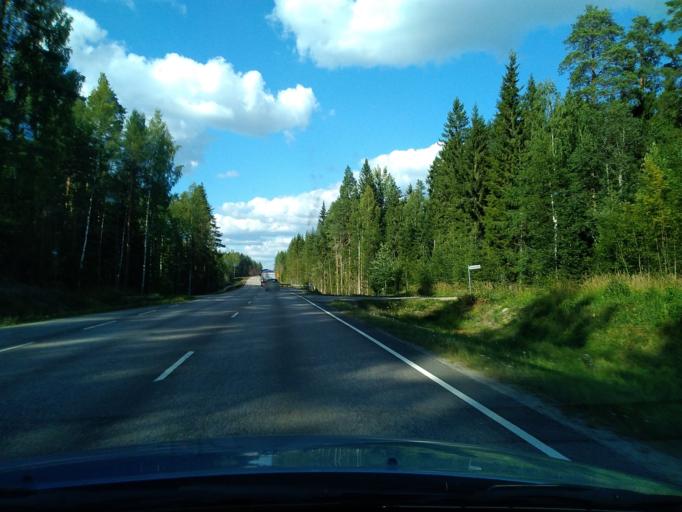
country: FI
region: Central Finland
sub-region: Keuruu
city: Keuruu
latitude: 62.1408
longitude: 24.7437
